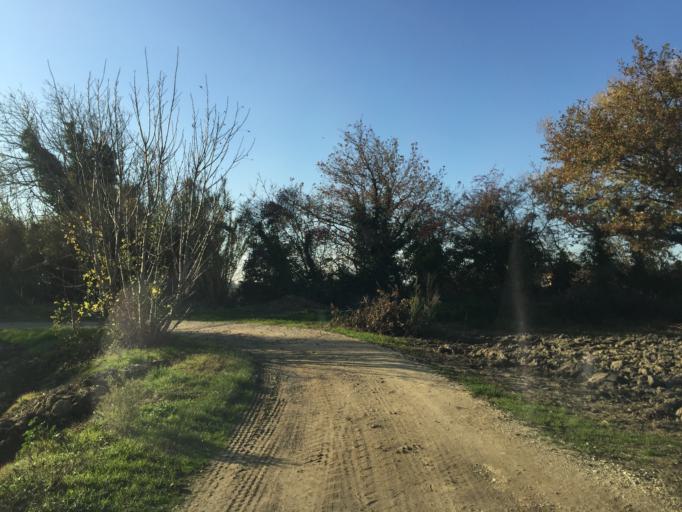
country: FR
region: Provence-Alpes-Cote d'Azur
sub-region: Departement du Vaucluse
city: Jonquieres
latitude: 44.1287
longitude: 4.9217
